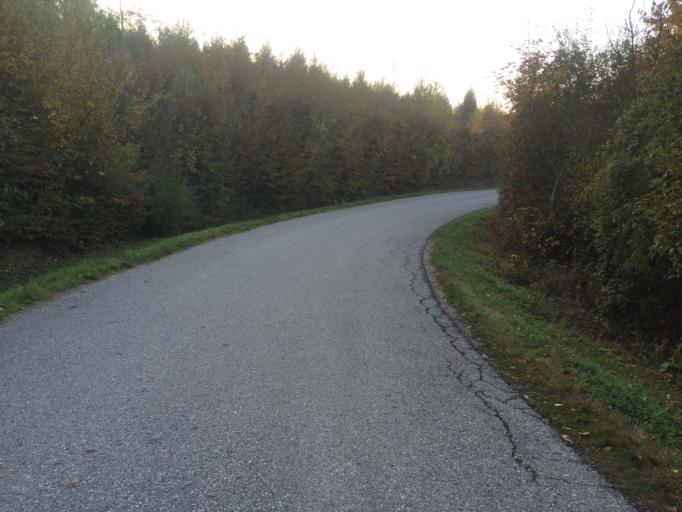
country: AT
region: Lower Austria
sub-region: Politischer Bezirk Wien-Umgebung
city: Gablitz
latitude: 48.2192
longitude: 16.1389
